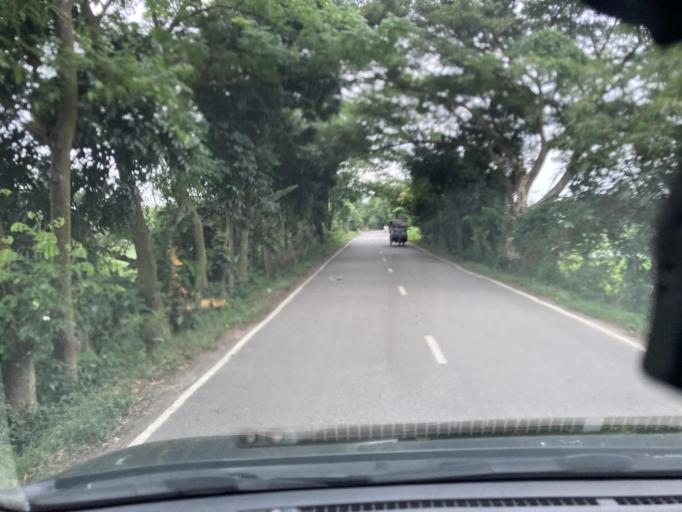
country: BD
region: Dhaka
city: Azimpur
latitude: 23.7790
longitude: 90.2076
